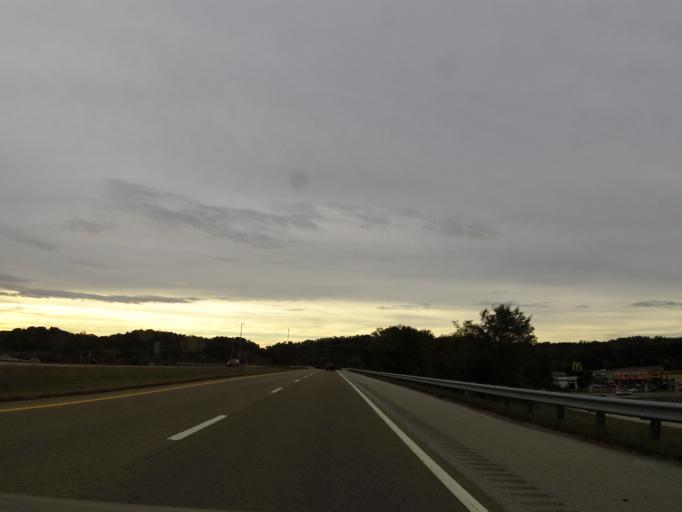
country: US
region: Tennessee
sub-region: Blount County
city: Alcoa
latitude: 35.8453
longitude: -83.9908
